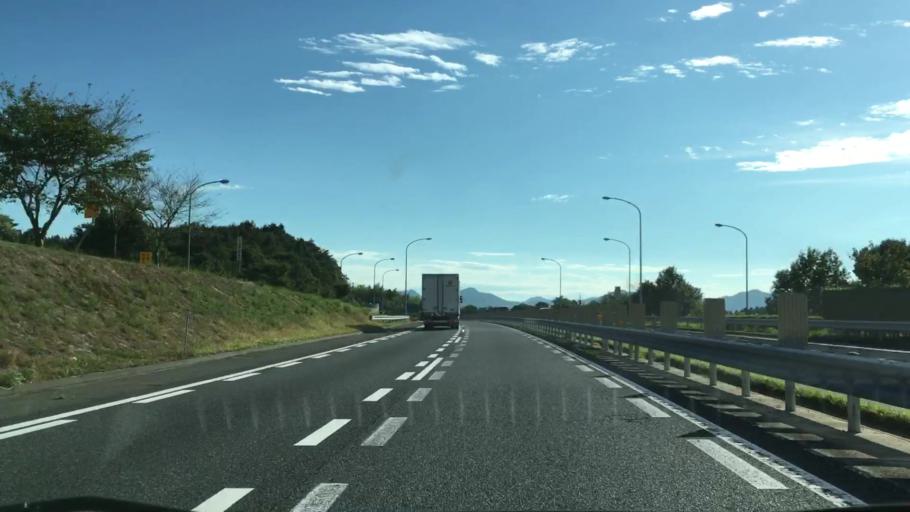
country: JP
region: Yamaguchi
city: Yanai
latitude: 34.0993
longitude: 132.1013
